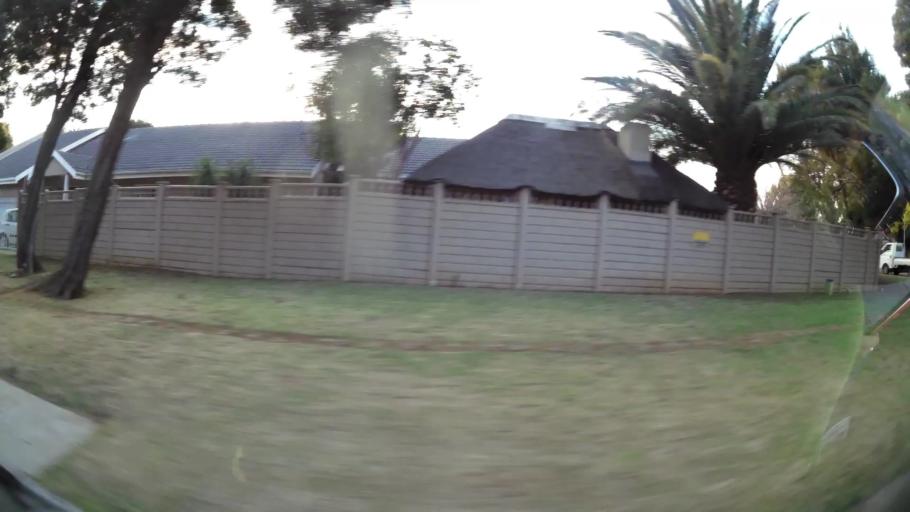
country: ZA
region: Gauteng
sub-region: Ekurhuleni Metropolitan Municipality
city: Benoni
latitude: -26.1675
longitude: 28.3038
